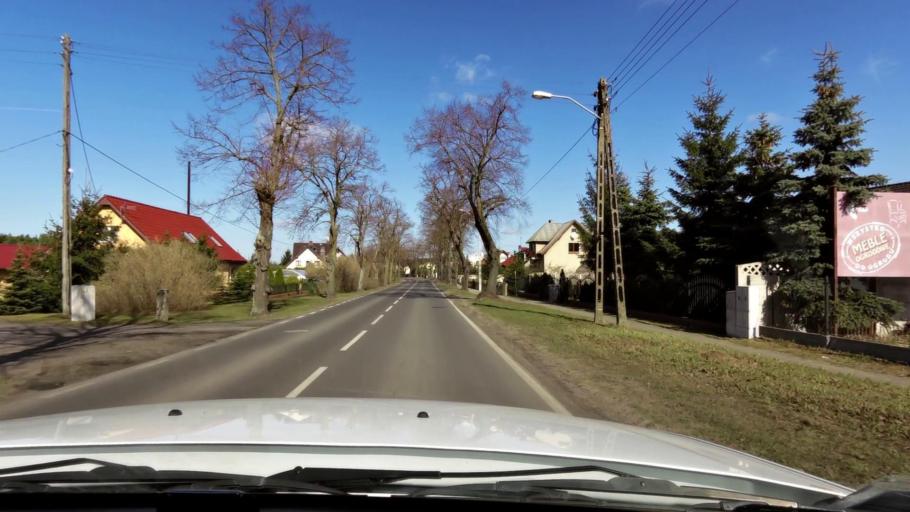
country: PL
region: West Pomeranian Voivodeship
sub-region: Powiat gryfinski
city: Gryfino
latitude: 53.2169
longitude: 14.4945
